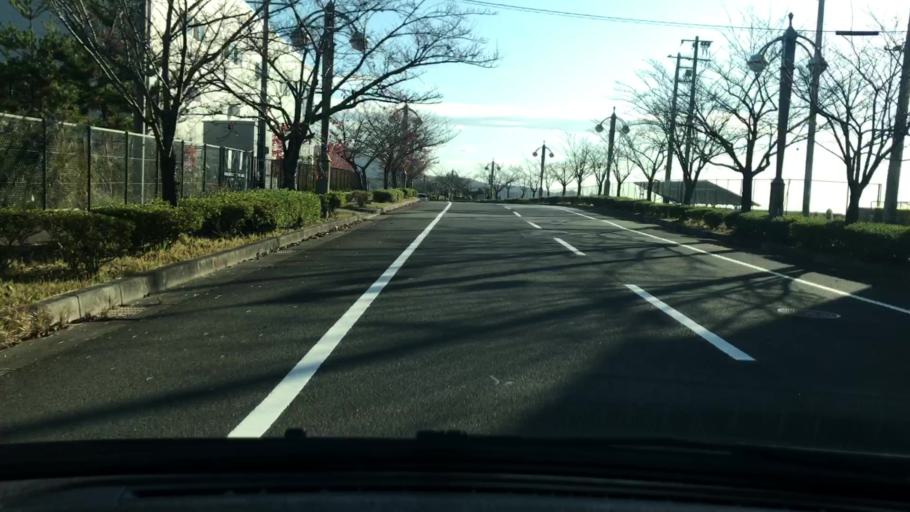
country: JP
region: Hyogo
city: Takarazuka
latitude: 34.8345
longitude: 135.3004
